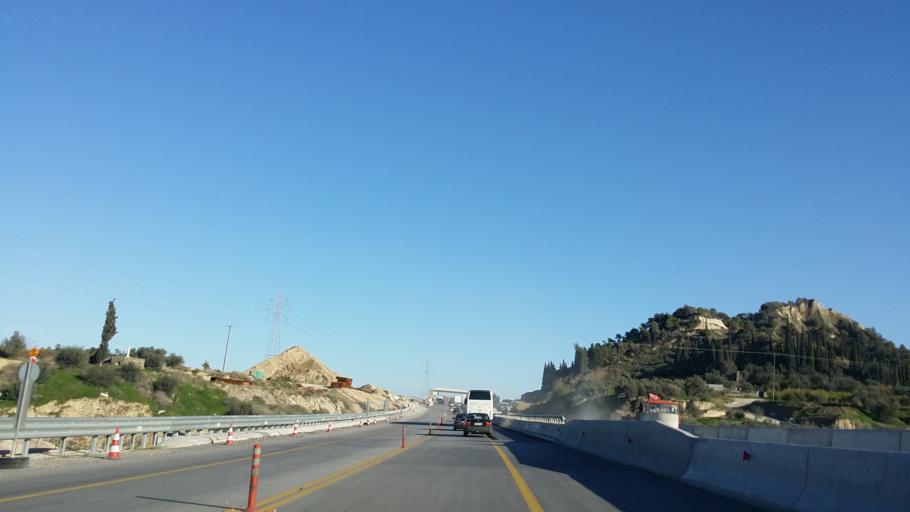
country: GR
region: West Greece
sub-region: Nomos Achaias
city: Aiyira
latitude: 38.1303
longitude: 22.4866
